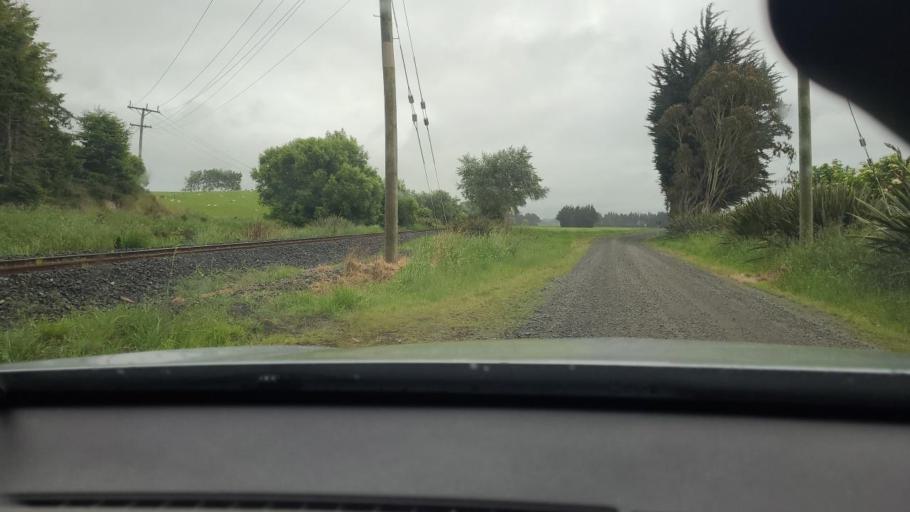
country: NZ
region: Southland
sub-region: Southland District
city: Riverton
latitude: -46.1905
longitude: 168.0403
